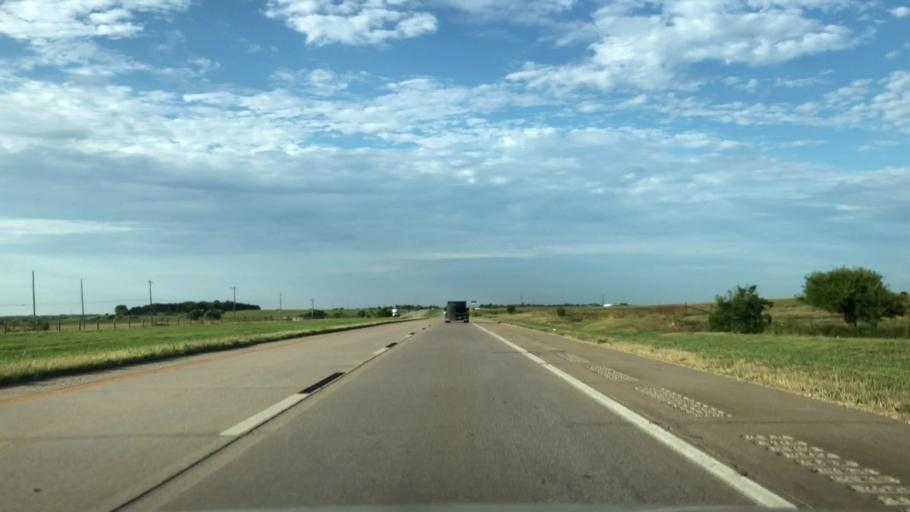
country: US
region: Oklahoma
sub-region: Osage County
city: Skiatook
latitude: 36.3901
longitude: -95.9206
